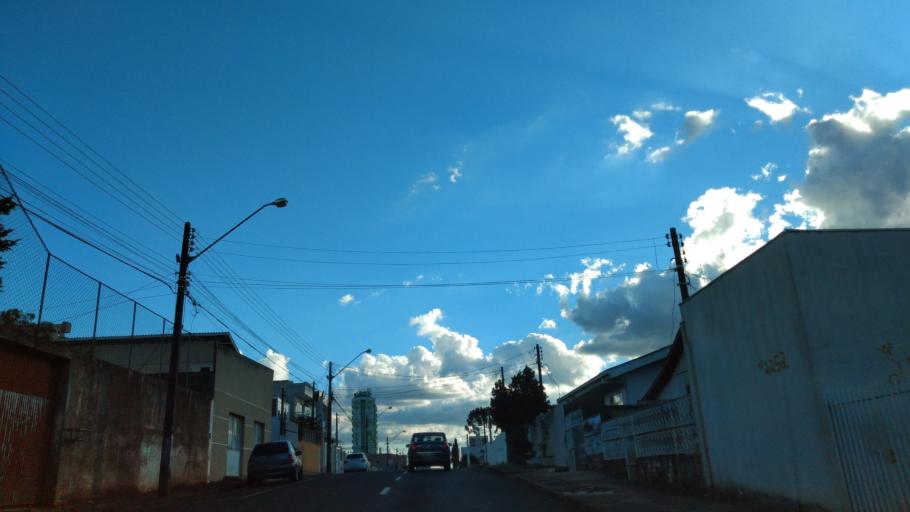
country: BR
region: Parana
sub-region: Guarapuava
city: Guarapuava
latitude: -25.3858
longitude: -51.4611
